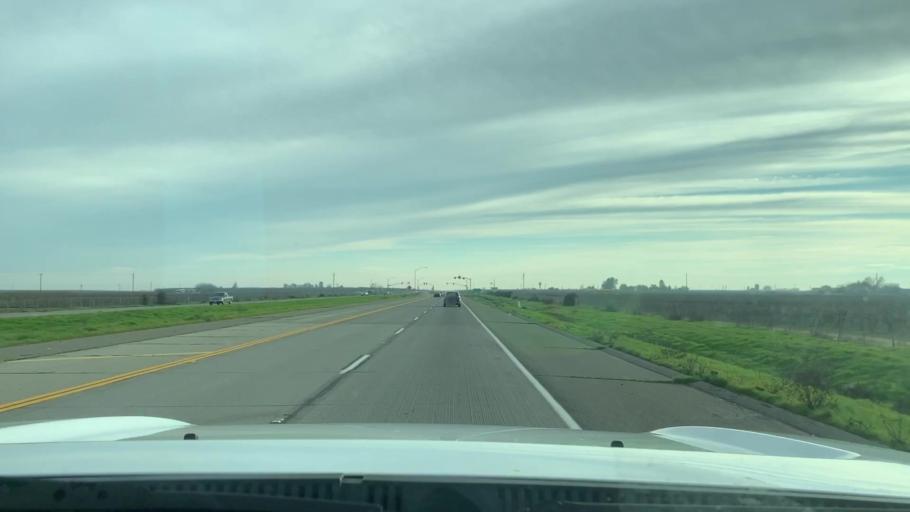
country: US
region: California
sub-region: Fresno County
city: Caruthers
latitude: 36.5520
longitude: -119.7863
